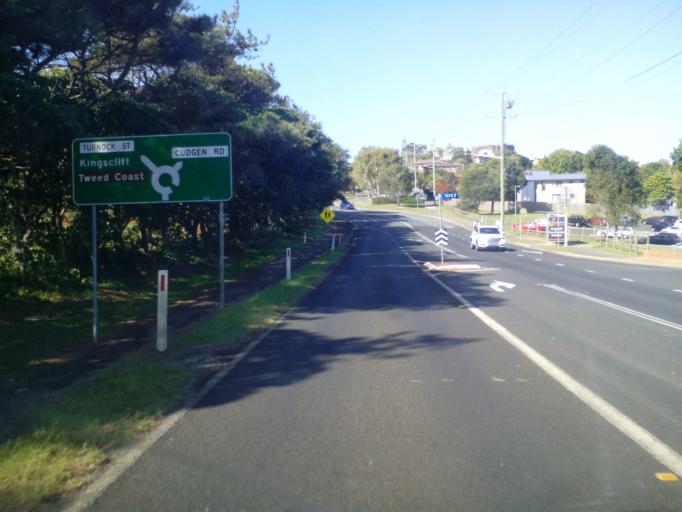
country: AU
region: New South Wales
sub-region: Tweed
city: Kingscliff
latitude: -28.2637
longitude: 153.5690
